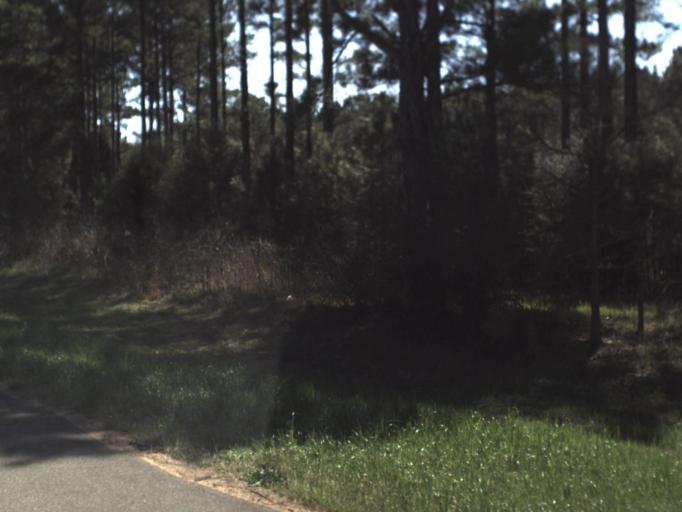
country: US
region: Florida
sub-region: Jackson County
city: Marianna
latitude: 30.8355
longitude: -85.3402
